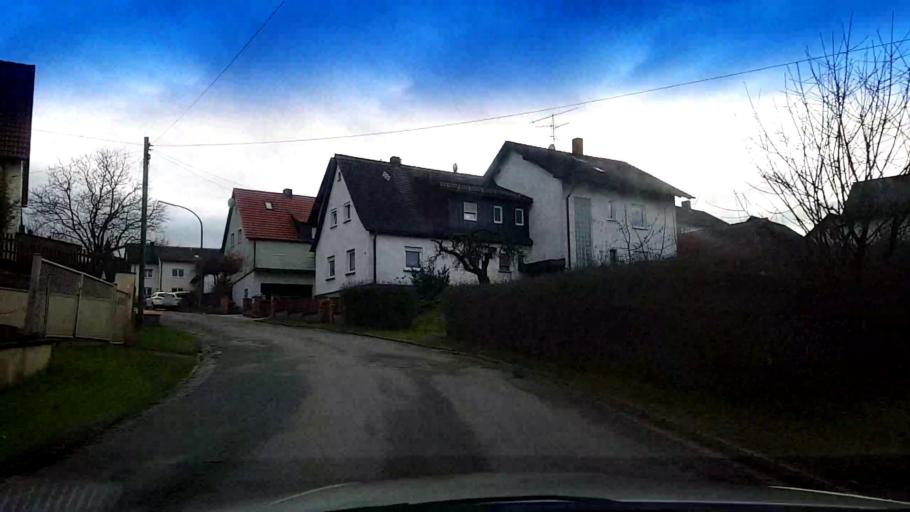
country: DE
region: Bavaria
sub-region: Upper Franconia
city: Litzendorf
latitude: 49.9076
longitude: 11.0027
